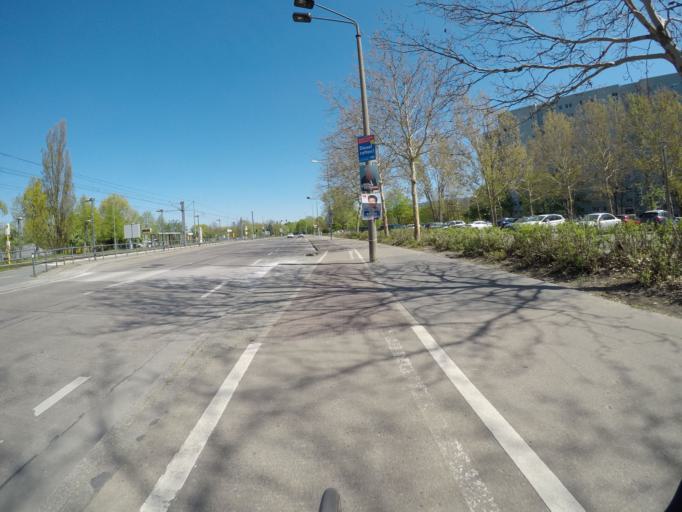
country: DE
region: Berlin
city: Wartenberg
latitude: 52.5690
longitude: 13.5249
